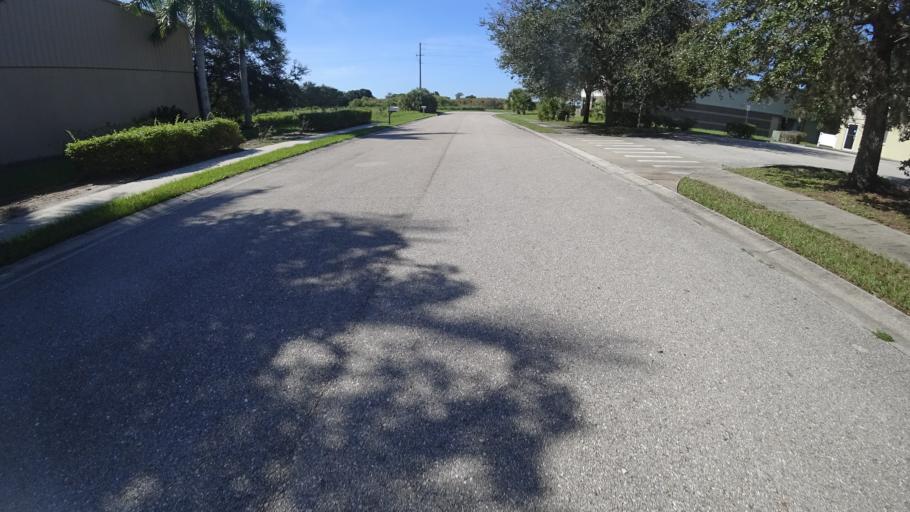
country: US
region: Florida
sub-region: Manatee County
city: Whitfield
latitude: 27.4121
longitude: -82.5340
